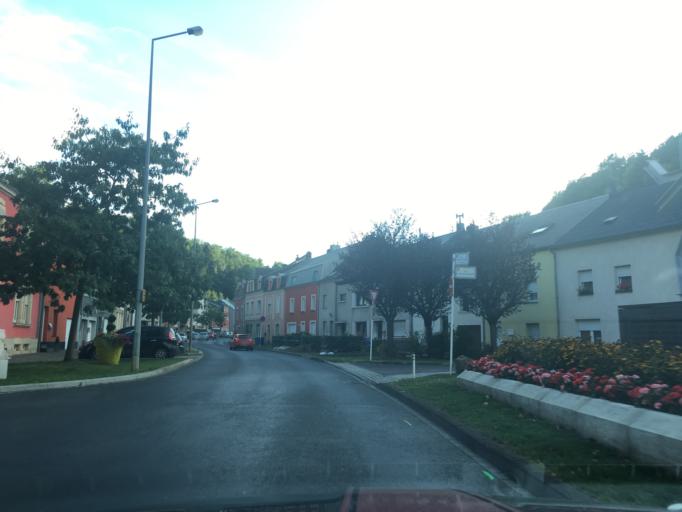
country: LU
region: Luxembourg
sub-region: Canton d'Esch-sur-Alzette
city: Differdange
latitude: 49.5205
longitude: 5.8823
